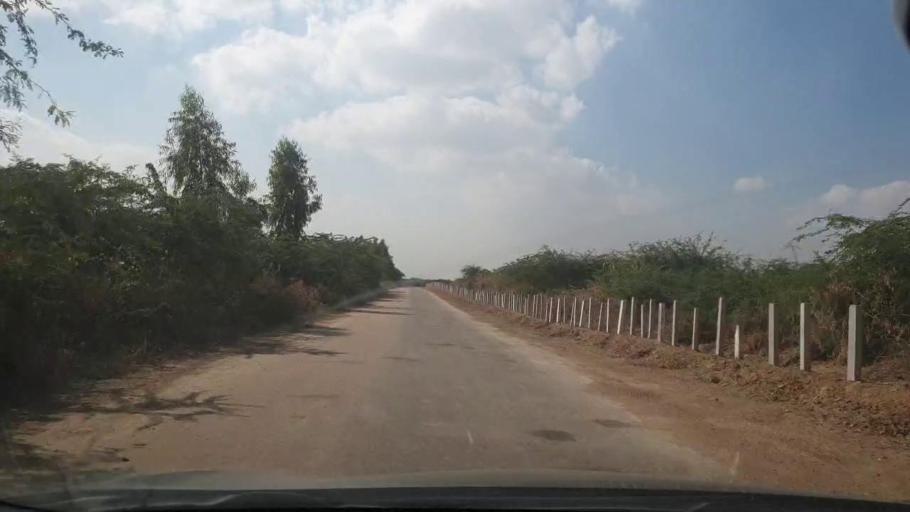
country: PK
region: Sindh
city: Malir Cantonment
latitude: 25.0232
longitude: 67.3569
